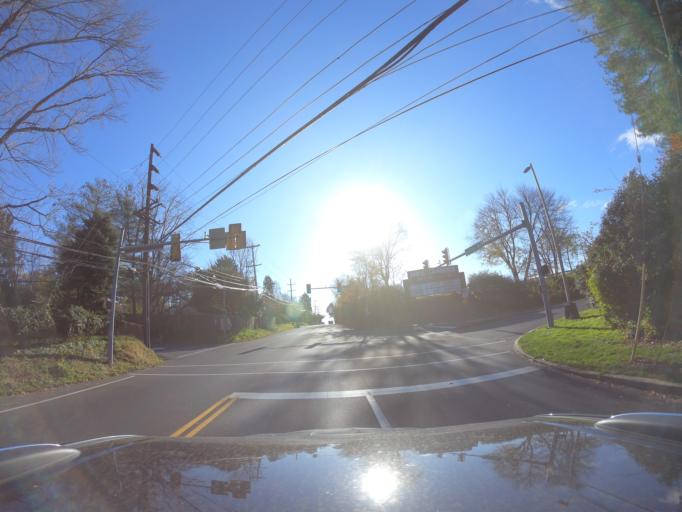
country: US
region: Pennsylvania
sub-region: Bucks County
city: Trevose
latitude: 40.1422
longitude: -74.9536
